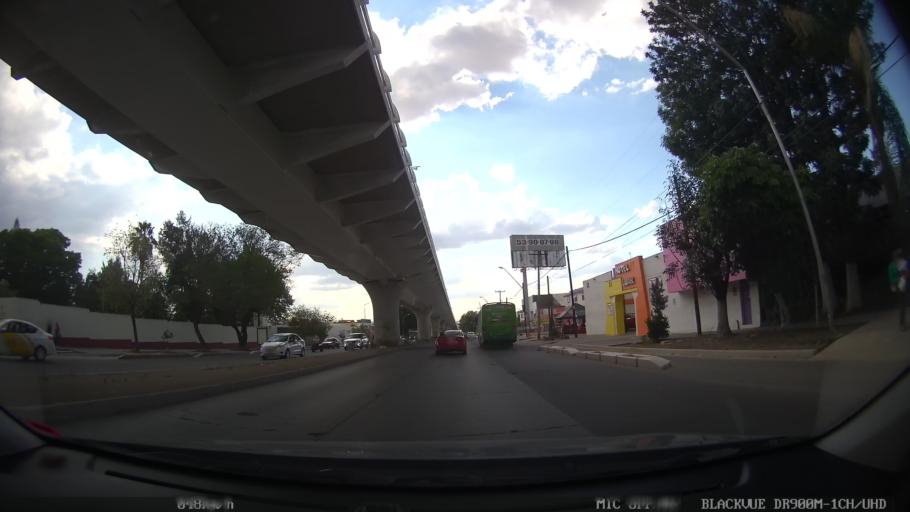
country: MX
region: Jalisco
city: Tlaquepaque
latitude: 20.6540
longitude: -103.3149
